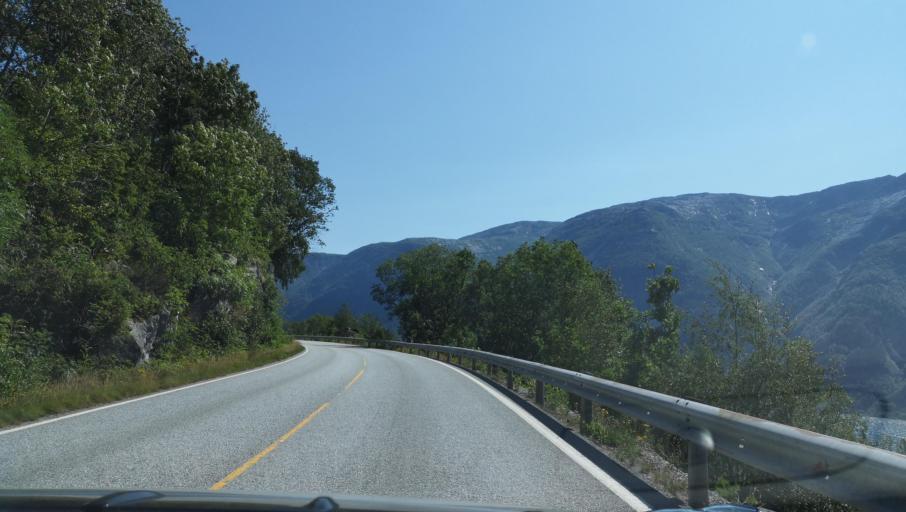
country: NO
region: Hordaland
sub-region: Ulvik
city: Ulvik
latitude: 60.4862
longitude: 6.8740
